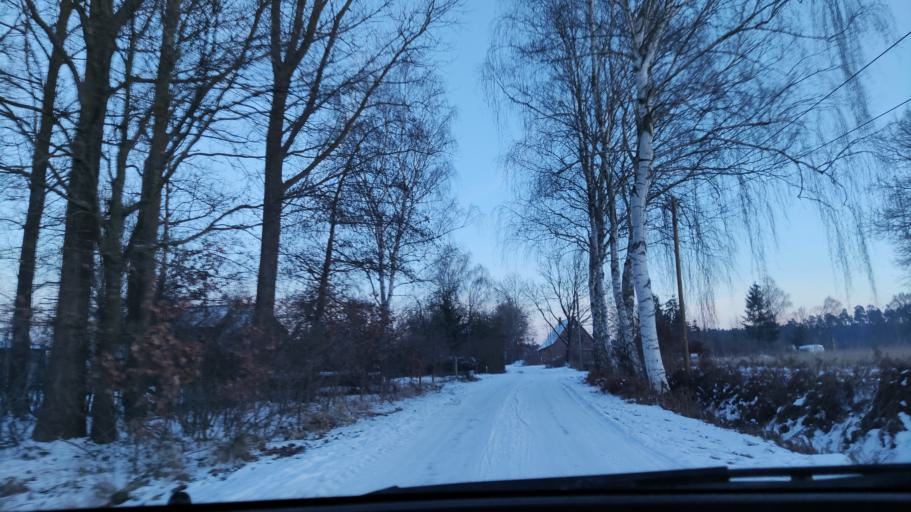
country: DE
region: Lower Saxony
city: Neetze
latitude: 53.2950
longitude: 10.6709
